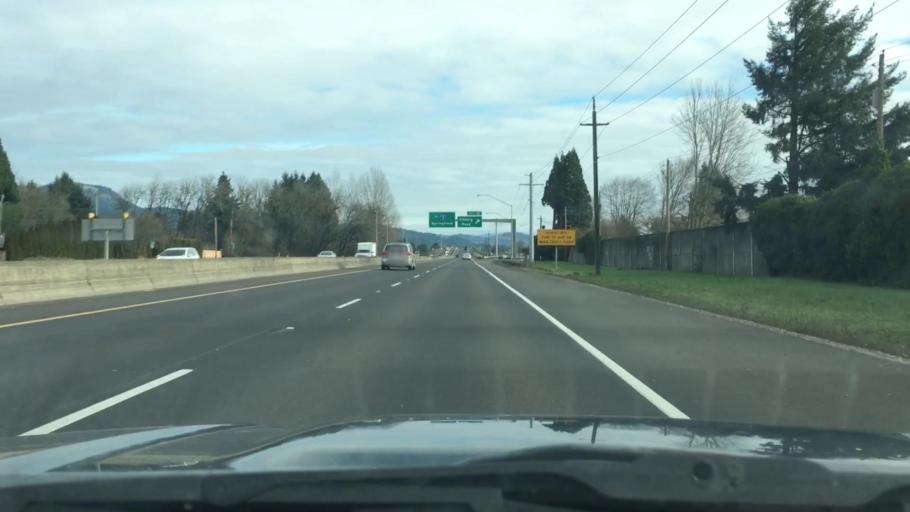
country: US
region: Oregon
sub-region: Lane County
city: Eugene
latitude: 44.0879
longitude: -123.0777
